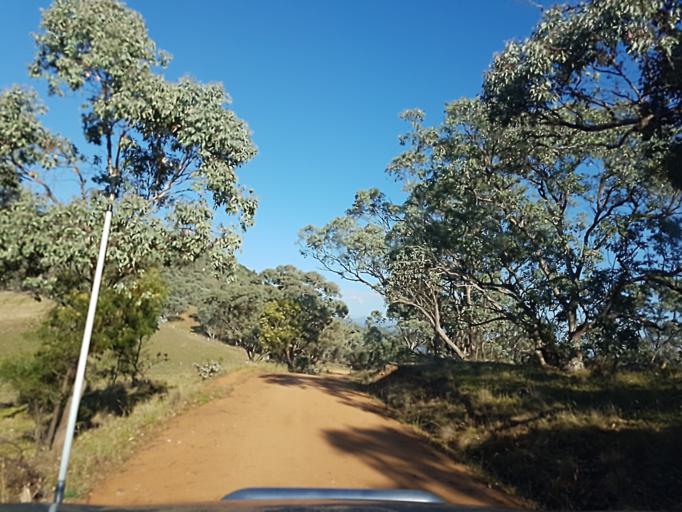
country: AU
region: New South Wales
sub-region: Snowy River
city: Jindabyne
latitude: -36.9510
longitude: 148.3532
